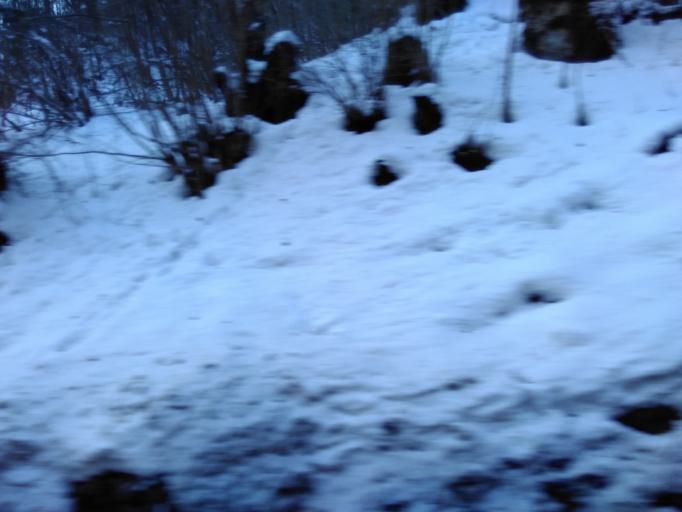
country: CH
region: Schwyz
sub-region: Bezirk March
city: Vorderthal
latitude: 47.1517
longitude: 8.8963
